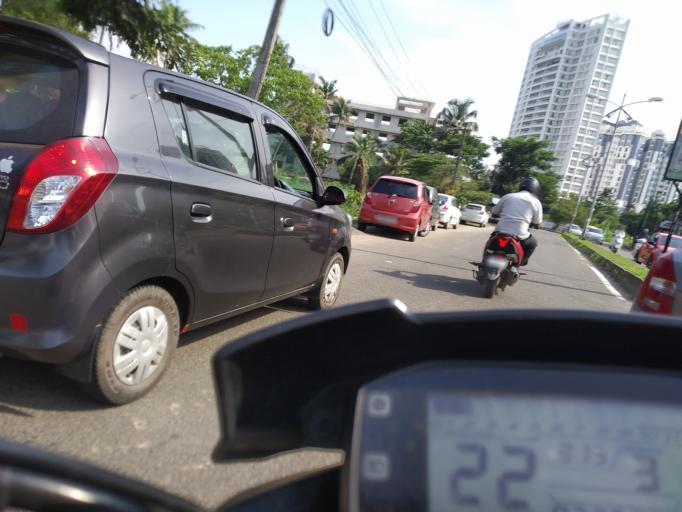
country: IN
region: Kerala
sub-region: Ernakulam
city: Cochin
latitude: 9.9884
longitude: 76.3020
